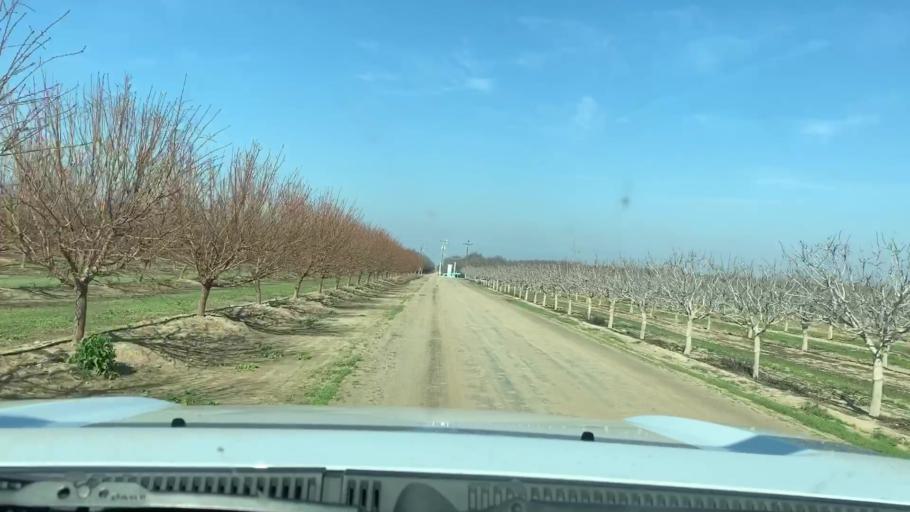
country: US
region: California
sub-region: Kern County
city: Lost Hills
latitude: 35.6139
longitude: -119.5358
